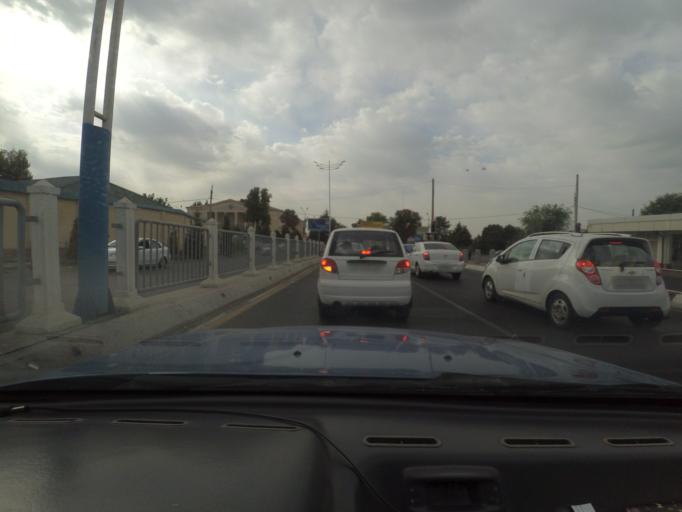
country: UZ
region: Toshkent
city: Salor
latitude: 41.3674
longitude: 69.4160
